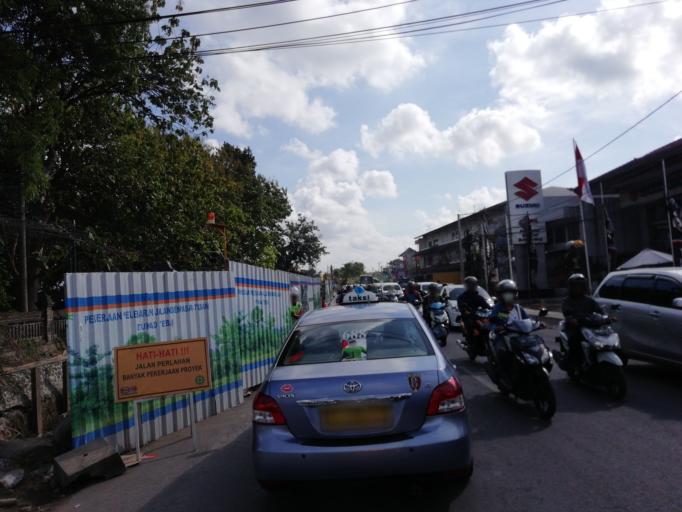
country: ID
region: Bali
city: Kuta
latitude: -8.6986
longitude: 115.1854
